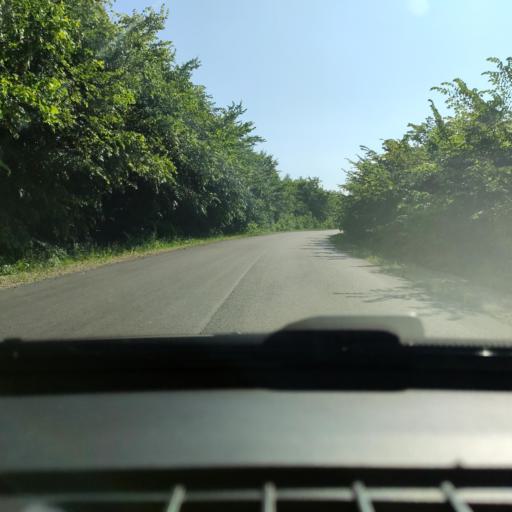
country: RU
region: Voronezj
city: Anna
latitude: 51.6288
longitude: 40.3449
